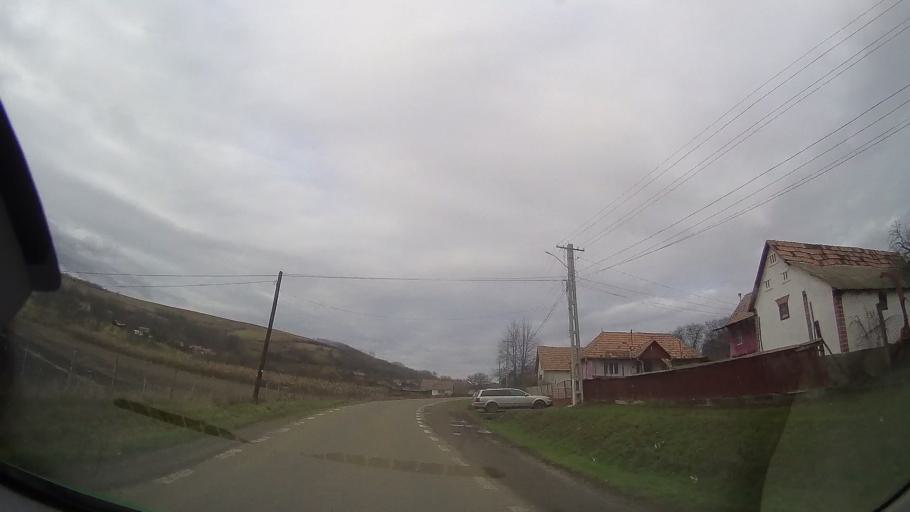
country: RO
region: Mures
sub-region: Comuna Cozma
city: Cozma
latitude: 46.8039
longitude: 24.5295
